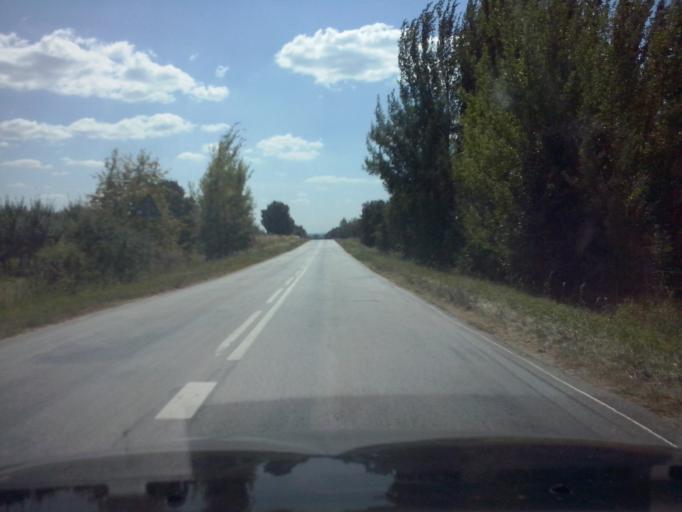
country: PL
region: Swietokrzyskie
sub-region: Powiat staszowski
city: Szydlow
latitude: 50.6050
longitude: 21.0095
